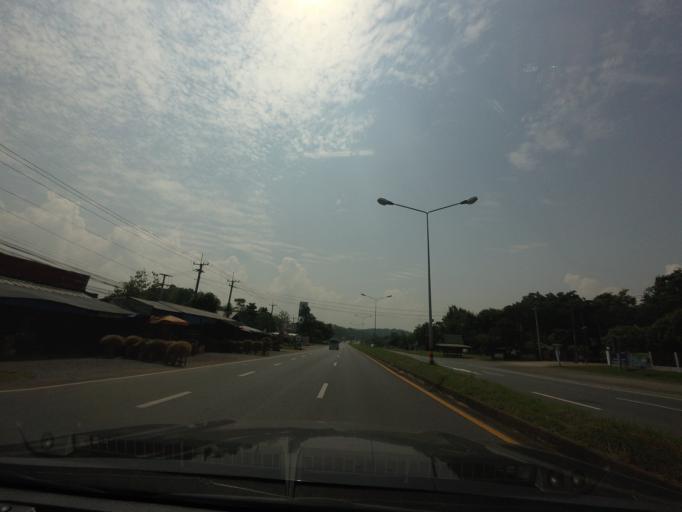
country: TH
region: Phrae
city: Den Chai
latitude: 17.9584
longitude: 100.0676
